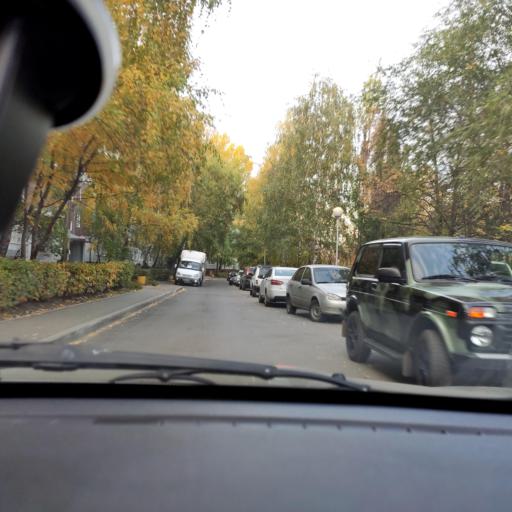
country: RU
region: Samara
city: Tol'yatti
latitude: 53.5402
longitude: 49.3195
